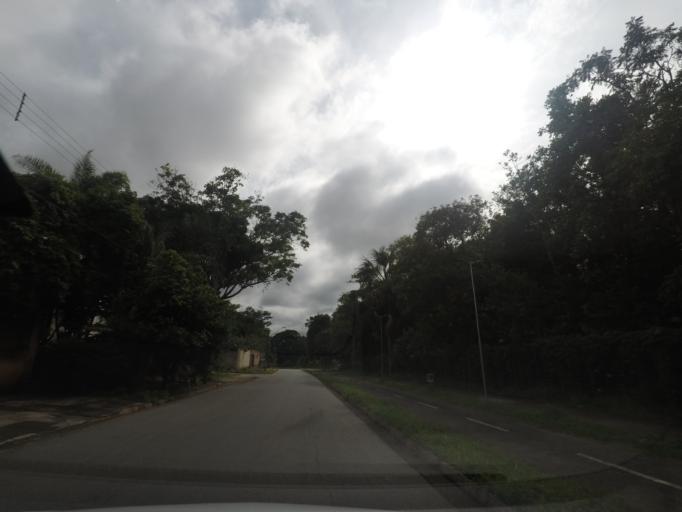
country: BR
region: Goias
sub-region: Goiania
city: Goiania
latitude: -16.7399
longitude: -49.3221
